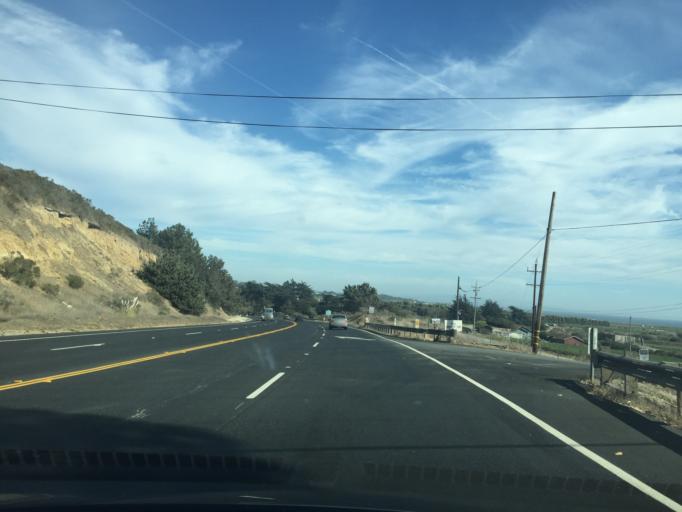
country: US
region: California
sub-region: Santa Cruz County
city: Santa Cruz
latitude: 36.9615
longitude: -122.0957
